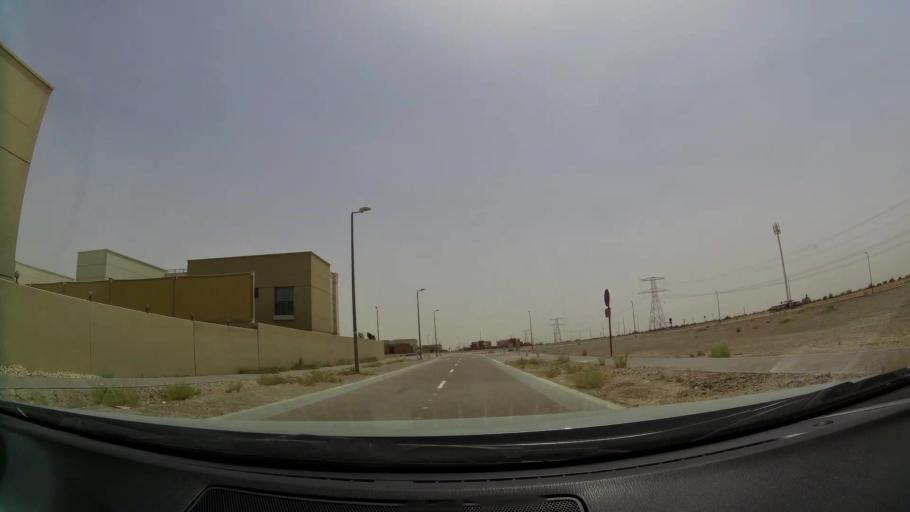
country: AE
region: Abu Dhabi
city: Al Ain
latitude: 24.1463
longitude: 55.6210
